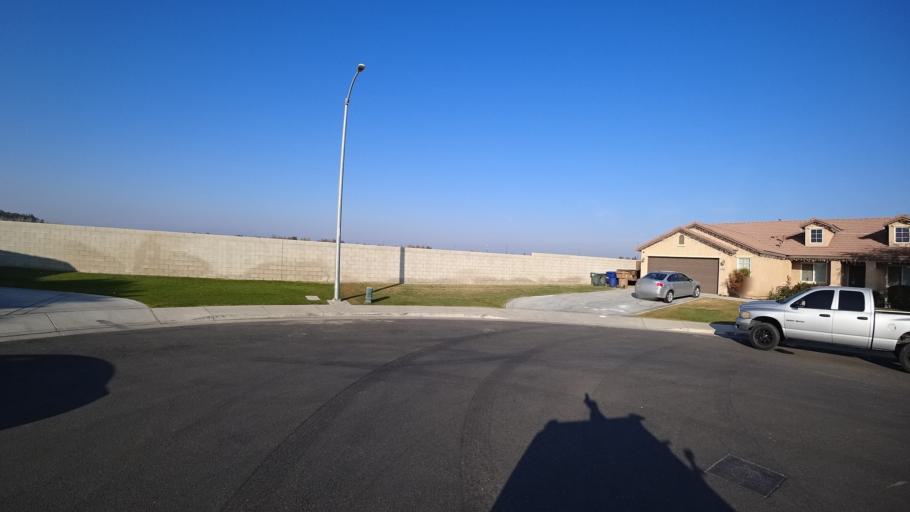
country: US
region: California
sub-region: Kern County
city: Greenacres
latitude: 35.2947
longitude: -119.1230
